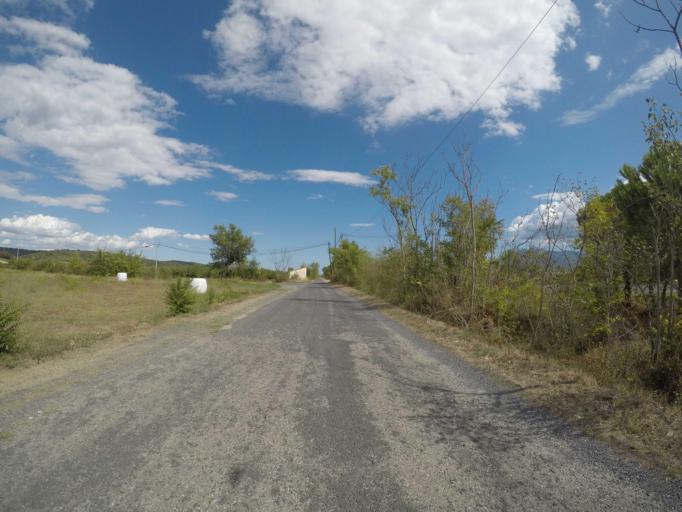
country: FR
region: Languedoc-Roussillon
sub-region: Departement des Pyrenees-Orientales
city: Sant Joan de Pladecorts
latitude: 42.5068
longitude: 2.7684
